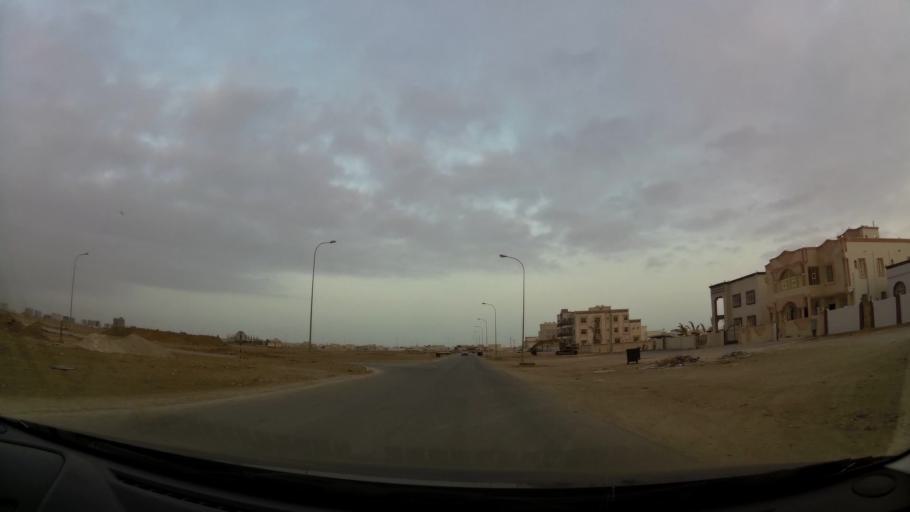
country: OM
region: Zufar
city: Salalah
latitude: 17.0271
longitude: 54.0139
